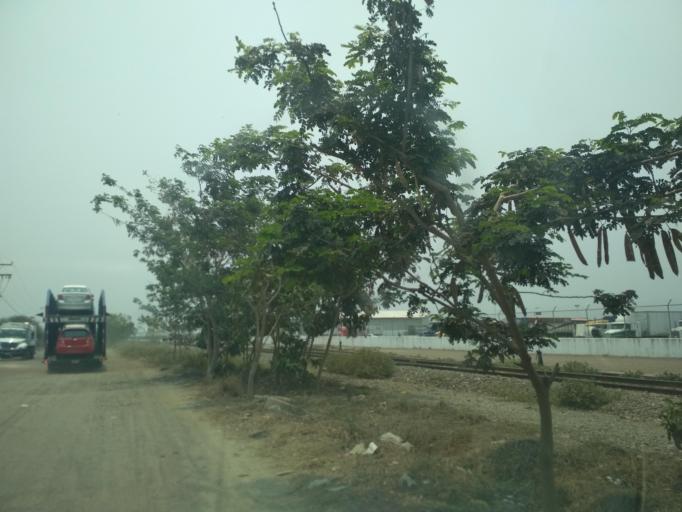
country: MX
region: Veracruz
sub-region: Veracruz
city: Delfino Victoria (Santa Fe)
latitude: 19.2012
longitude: -96.2659
